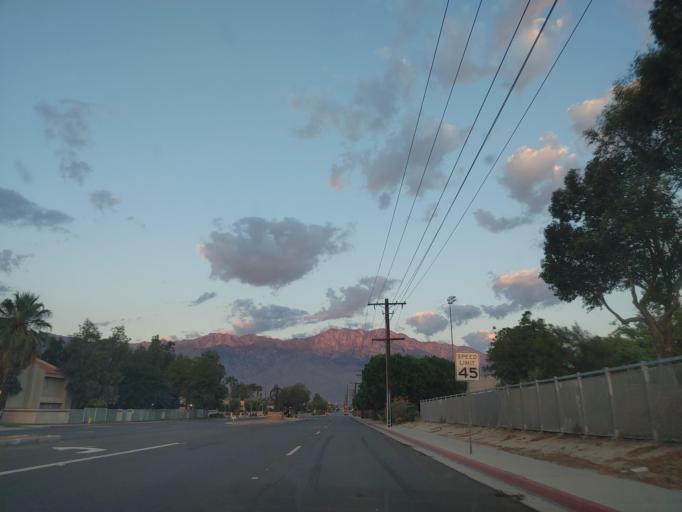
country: US
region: California
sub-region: Riverside County
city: Cathedral City
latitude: 33.8015
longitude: -116.4546
